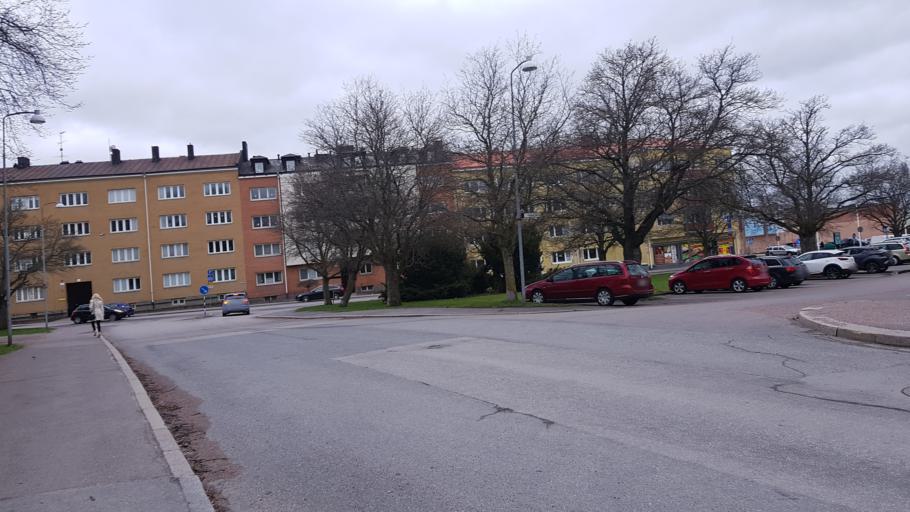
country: SE
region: OEstergoetland
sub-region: Norrkopings Kommun
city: Norrkoping
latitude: 58.5894
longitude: 16.2036
